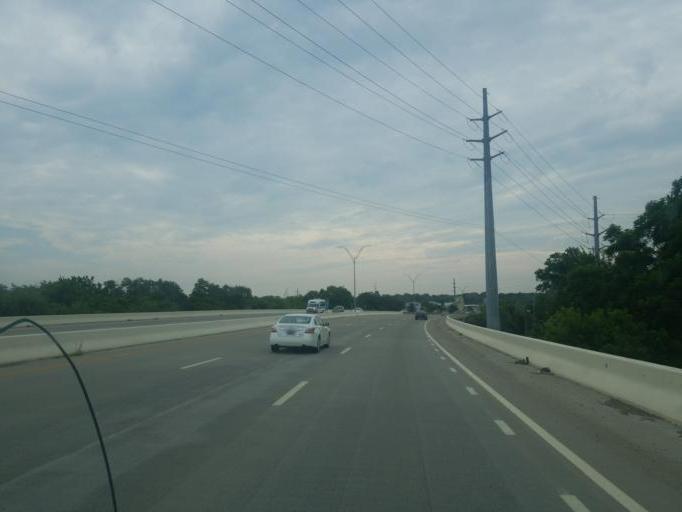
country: US
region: Ohio
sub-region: Stark County
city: Canton
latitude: 40.7879
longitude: -81.3665
